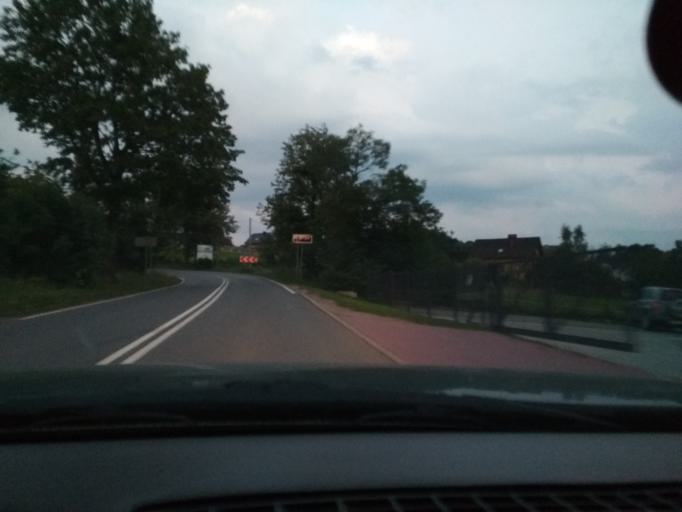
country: PL
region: Silesian Voivodeship
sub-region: Powiat bielski
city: Jasienica
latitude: 49.8370
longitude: 18.9436
